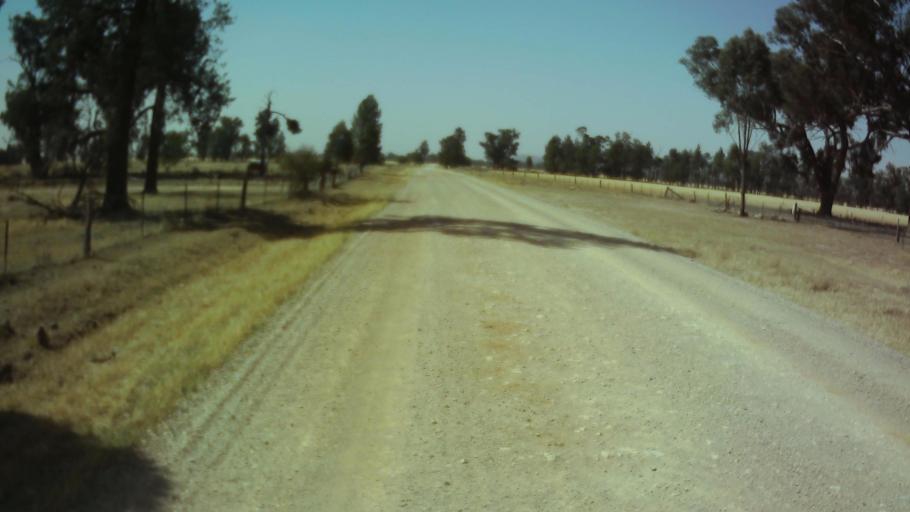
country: AU
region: New South Wales
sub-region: Weddin
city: Grenfell
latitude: -34.0197
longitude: 147.9147
